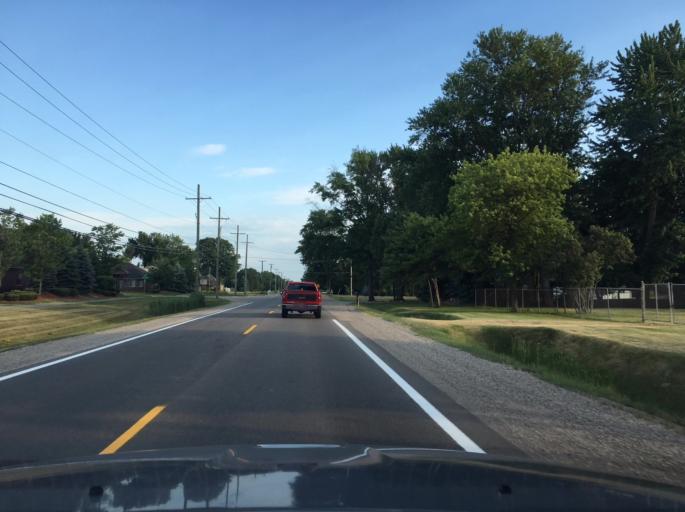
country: US
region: Michigan
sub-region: Macomb County
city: Mount Clemens
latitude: 42.6521
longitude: -82.8770
